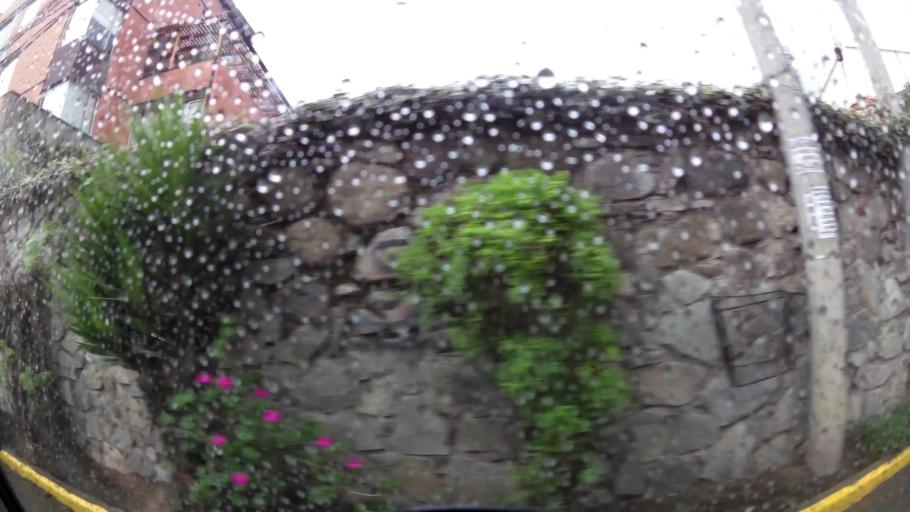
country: EC
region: Azuay
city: Cuenca
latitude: -2.8928
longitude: -79.0339
